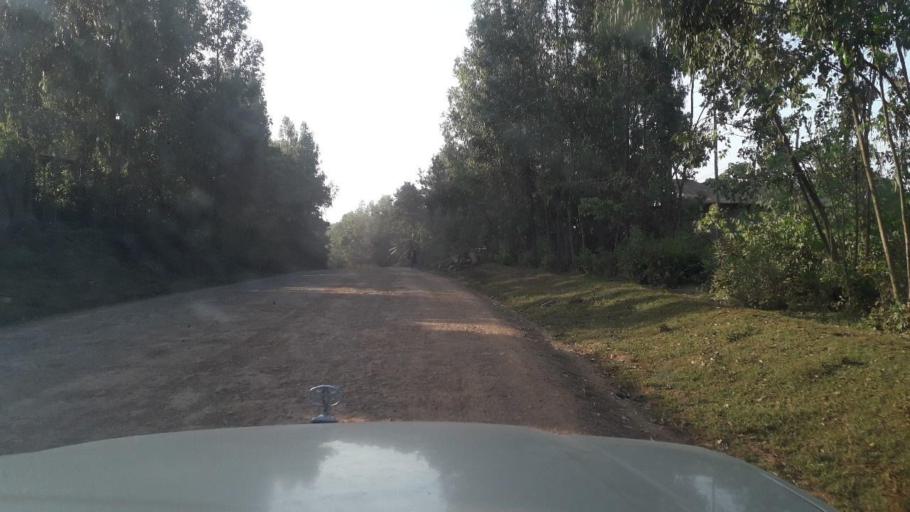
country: ET
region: Oromiya
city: Jima
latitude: 7.6007
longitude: 36.8446
